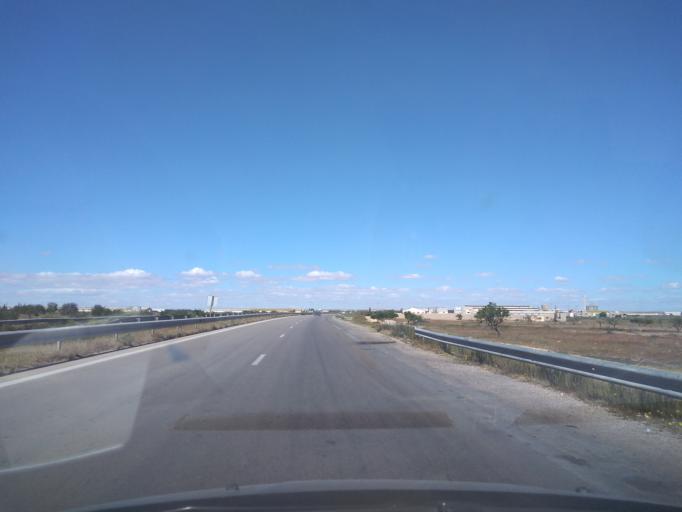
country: TN
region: Safaqis
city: Al Qarmadah
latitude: 34.8580
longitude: 10.7572
